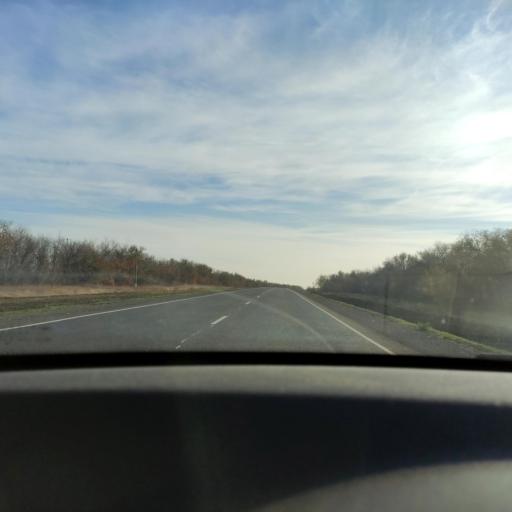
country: RU
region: Samara
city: Krasnoarmeyskoye
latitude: 52.8371
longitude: 50.0041
